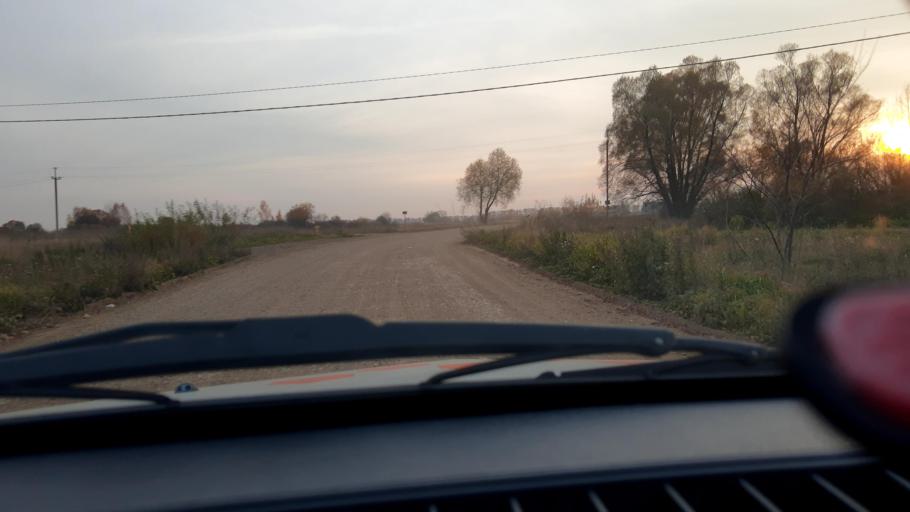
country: RU
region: Bashkortostan
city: Iglino
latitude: 54.7917
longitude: 56.3289
